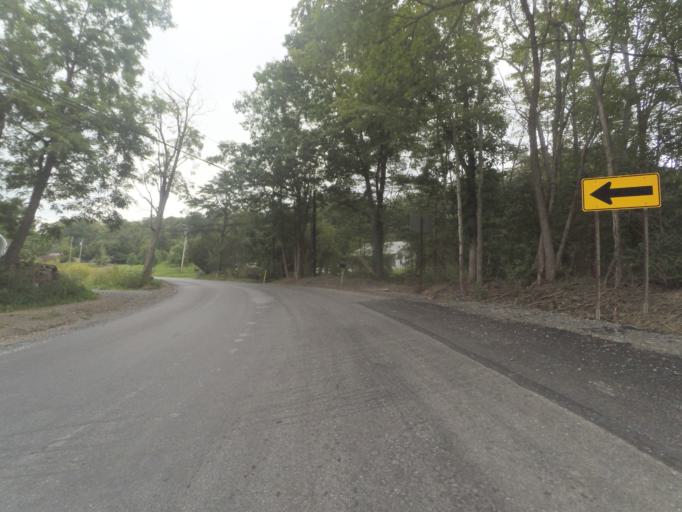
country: US
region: Pennsylvania
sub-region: Centre County
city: Zion
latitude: 41.0417
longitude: -77.6863
